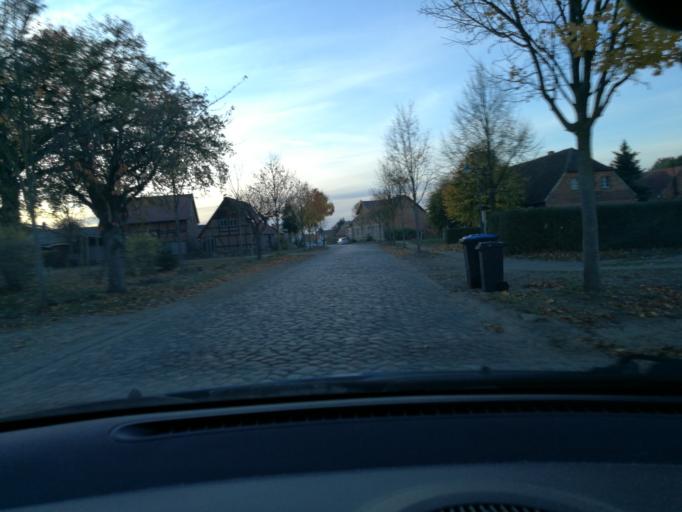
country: DE
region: Brandenburg
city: Cumlosen
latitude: 53.1000
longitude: 11.6940
